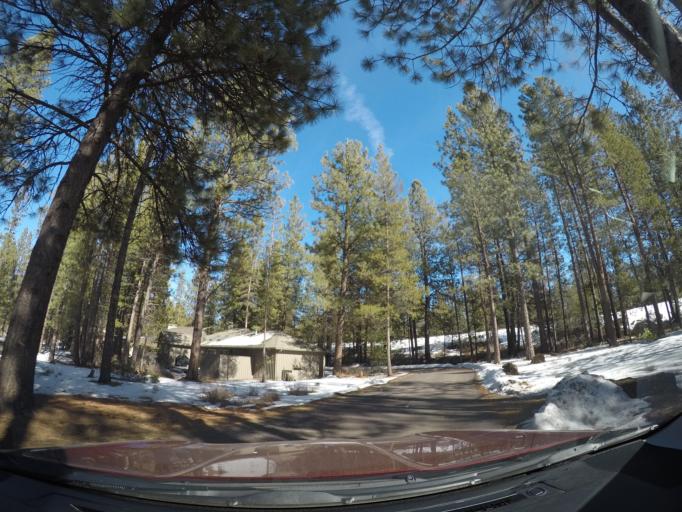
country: US
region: Oregon
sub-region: Deschutes County
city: Sunriver
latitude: 43.8787
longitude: -121.4287
